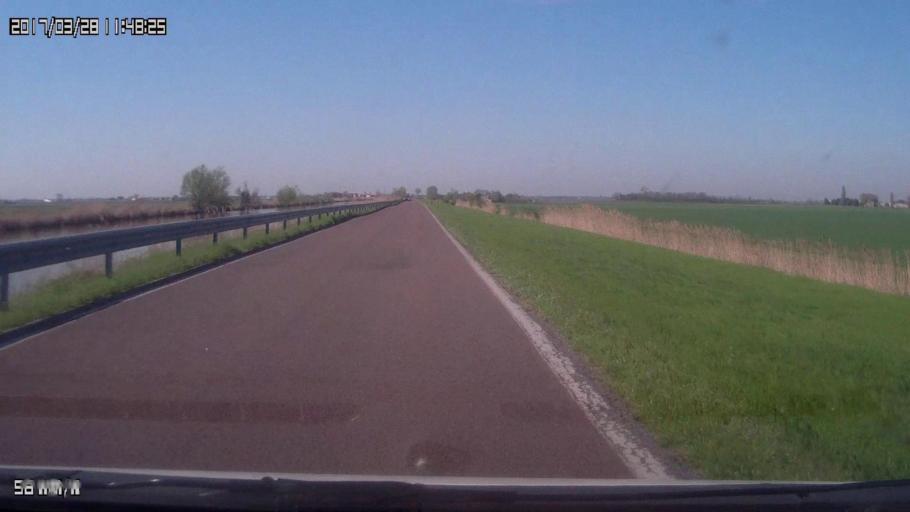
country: IT
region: Veneto
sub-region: Provincia di Venezia
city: Sant'Anna
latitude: 45.1618
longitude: 12.2230
